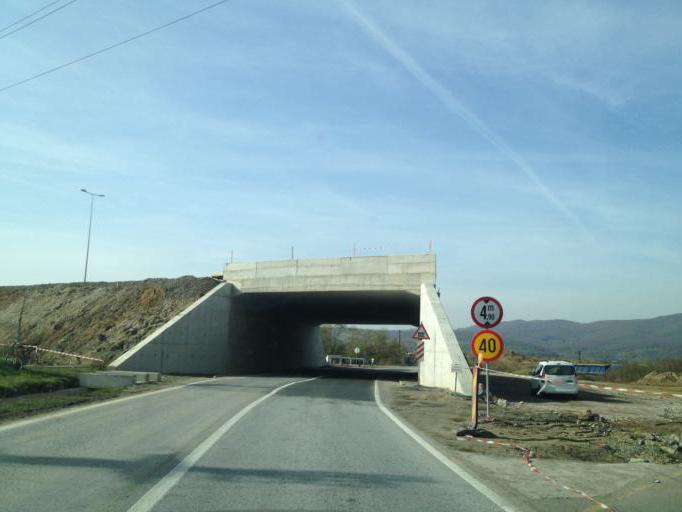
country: RO
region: Hunedoara
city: Lapugiu de Jos
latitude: 45.9130
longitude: 22.5158
